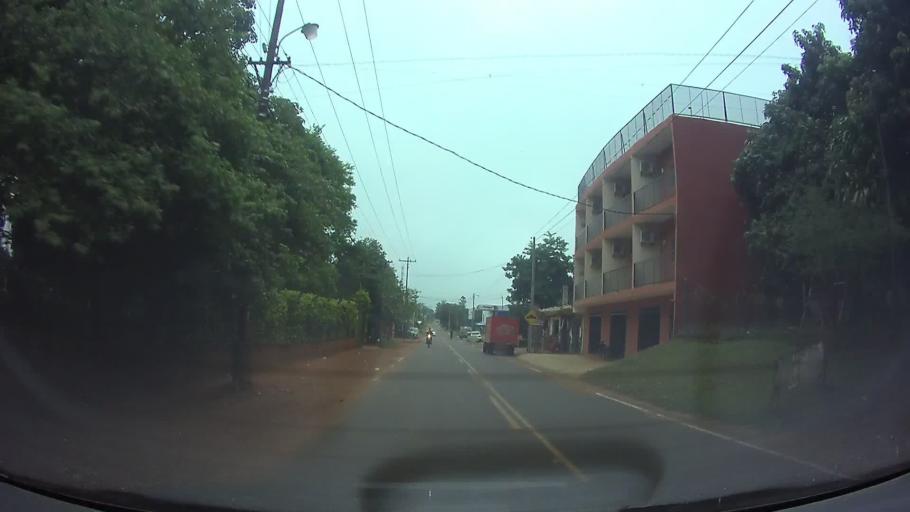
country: PY
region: Central
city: Itaugua
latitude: -25.3845
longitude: -57.3507
